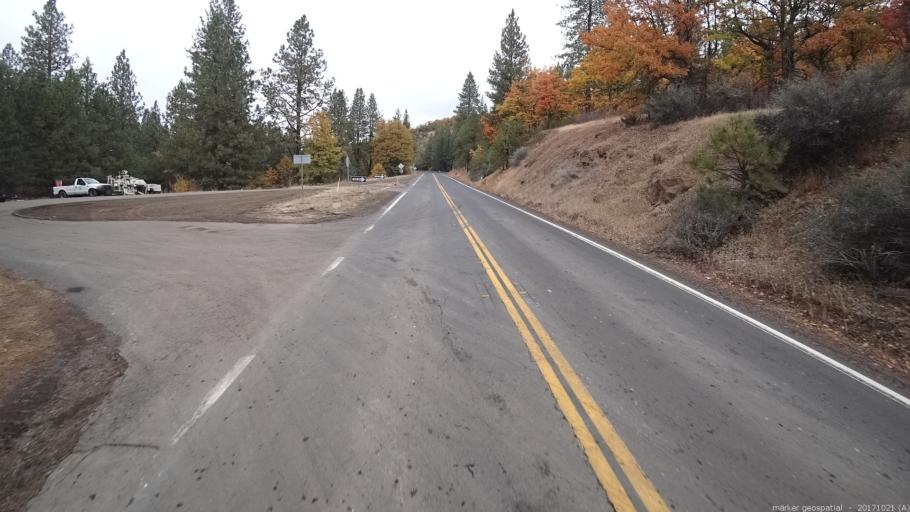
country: US
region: California
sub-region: Shasta County
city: Burney
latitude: 41.0186
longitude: -121.6214
